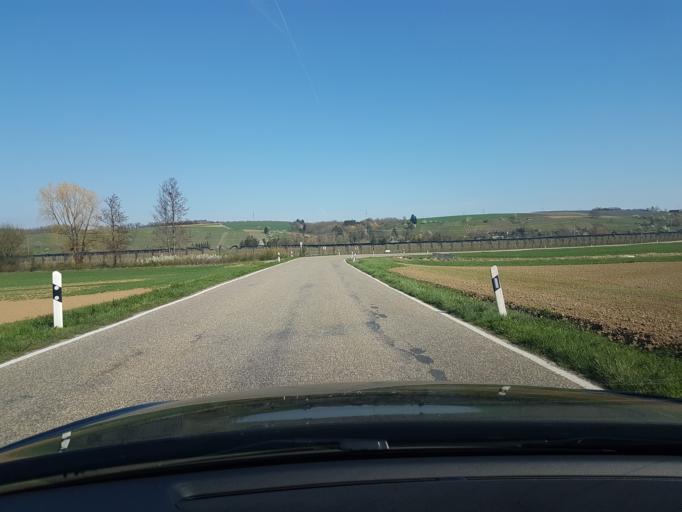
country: DE
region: Baden-Wuerttemberg
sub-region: Regierungsbezirk Stuttgart
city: Neuenstadt am Kocher
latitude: 49.2373
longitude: 9.3820
